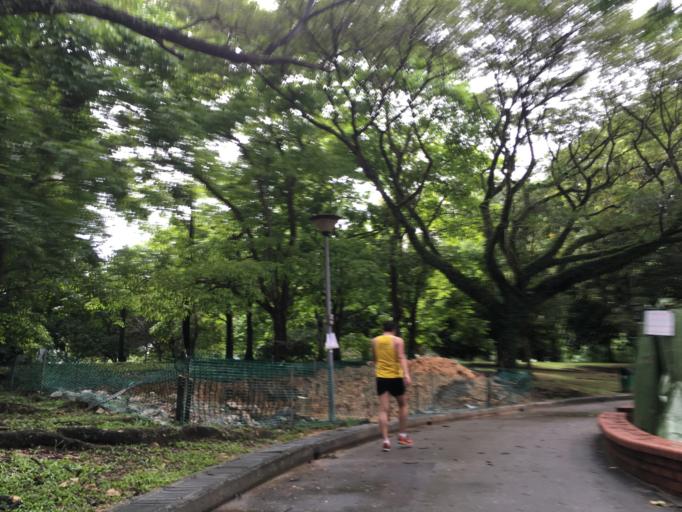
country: MY
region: Johor
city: Kampung Pasir Gudang Baru
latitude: 1.3785
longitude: 103.8996
